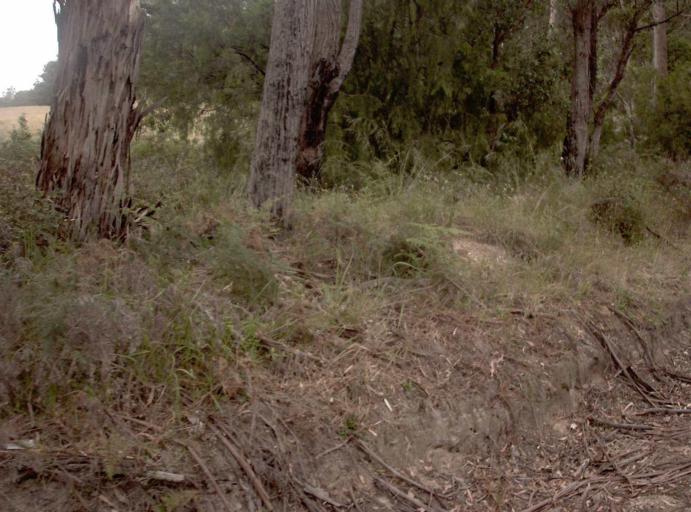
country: AU
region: Victoria
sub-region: East Gippsland
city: Bairnsdale
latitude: -37.7714
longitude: 147.5974
